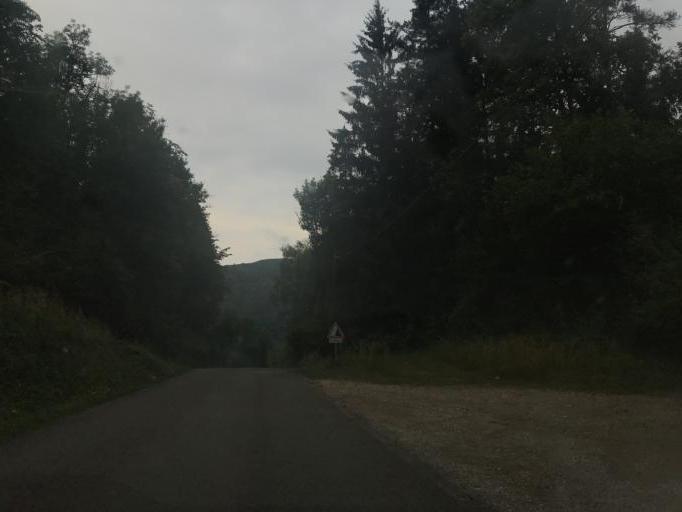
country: FR
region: Franche-Comte
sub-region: Departement du Jura
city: Lavans-les-Saint-Claude
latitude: 46.3498
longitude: 5.7684
